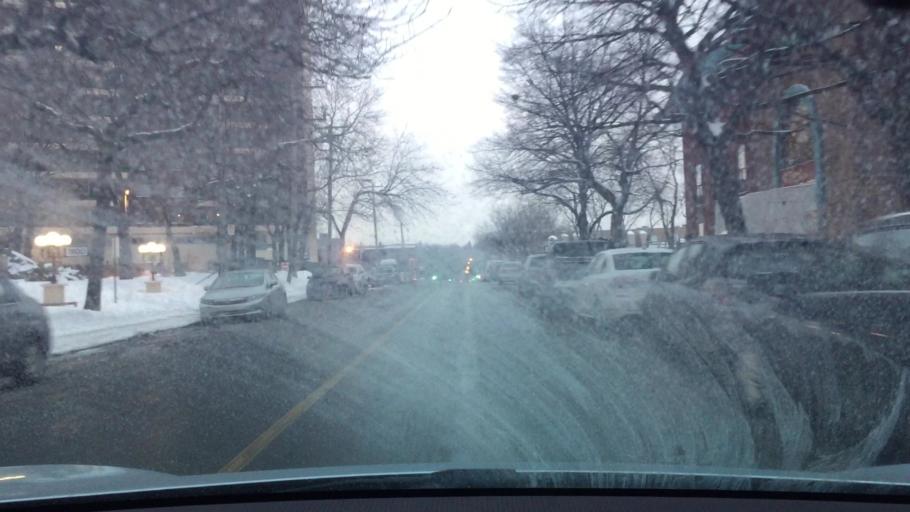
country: CA
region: Quebec
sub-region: Monteregie
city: Longueuil
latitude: 45.5339
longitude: -73.5493
